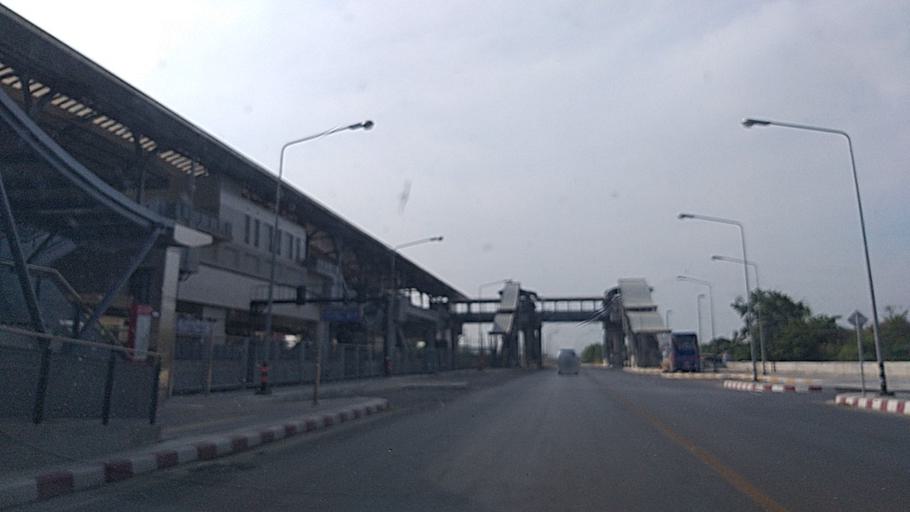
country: TH
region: Bangkok
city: Don Mueang
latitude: 13.9662
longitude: 100.6050
